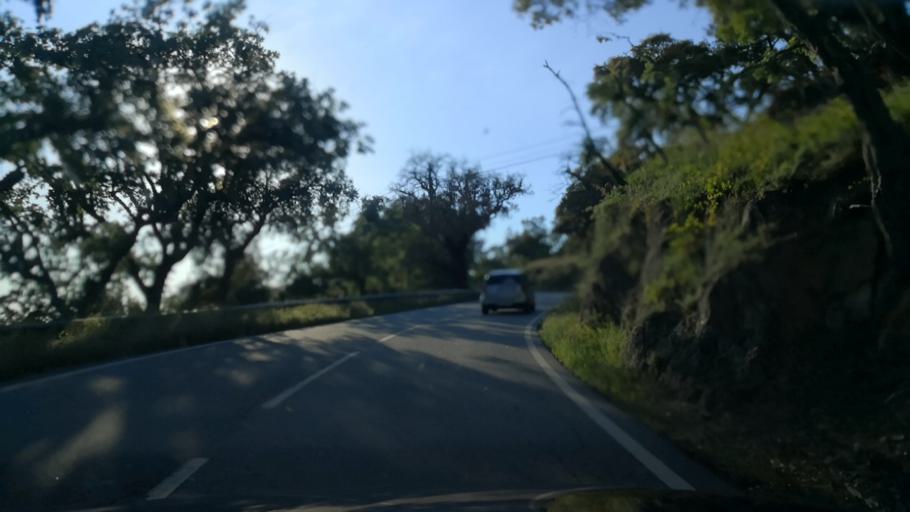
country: PT
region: Portalegre
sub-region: Portalegre
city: Portalegre
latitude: 39.3320
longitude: -7.4255
